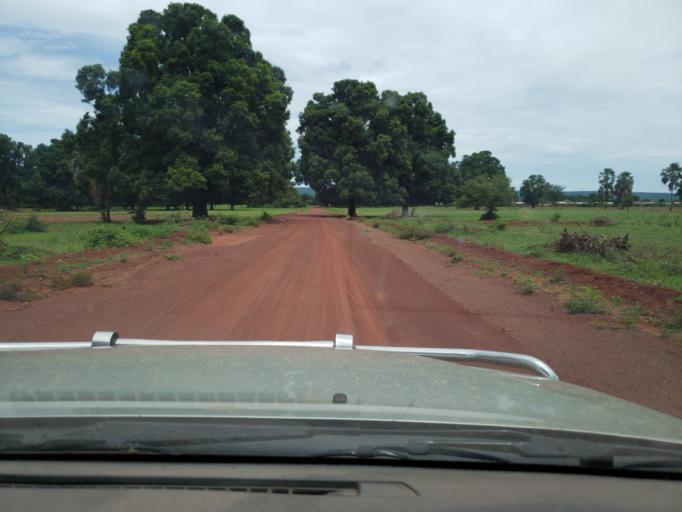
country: ML
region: Sikasso
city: Sikasso
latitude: 11.6746
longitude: -6.3359
